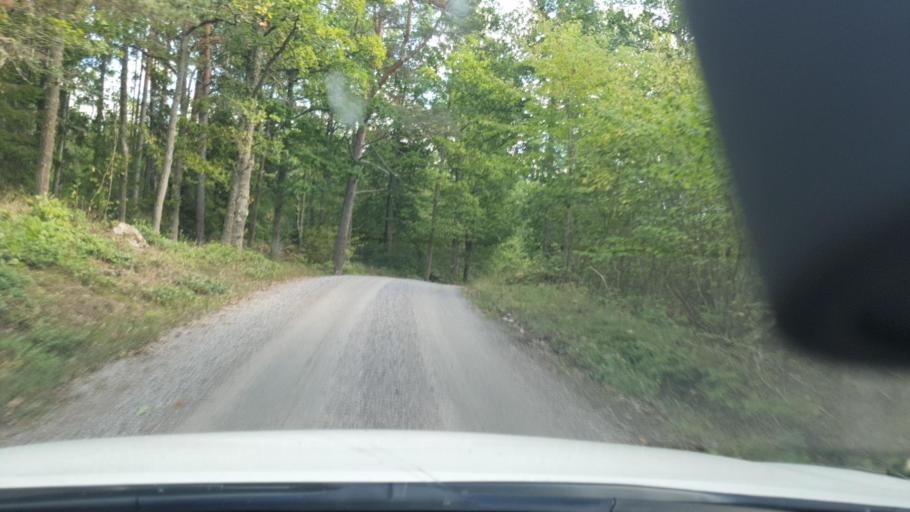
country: SE
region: Kalmar
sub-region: Vasterviks Kommun
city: Vaestervik
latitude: 57.7359
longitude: 16.4929
